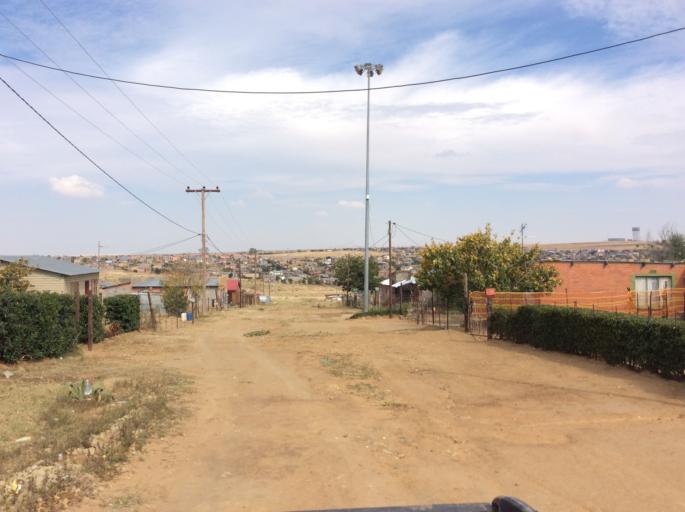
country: ZA
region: Orange Free State
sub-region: Xhariep District Municipality
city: Dewetsdorp
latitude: -29.5883
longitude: 26.6839
